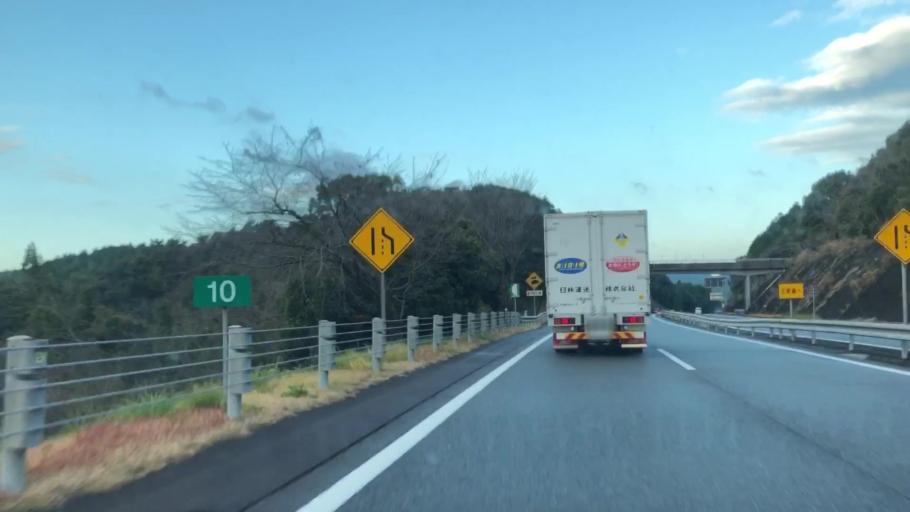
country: JP
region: Saga Prefecture
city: Imaricho-ko
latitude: 33.1550
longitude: 129.8880
